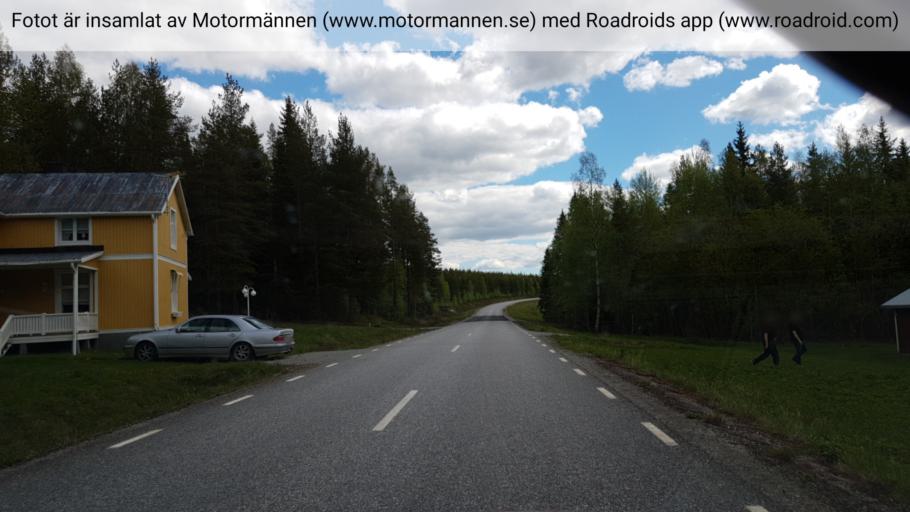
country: SE
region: Vaesterbotten
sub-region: Skelleftea Kommun
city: Langsele
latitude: 64.7231
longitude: 19.9684
